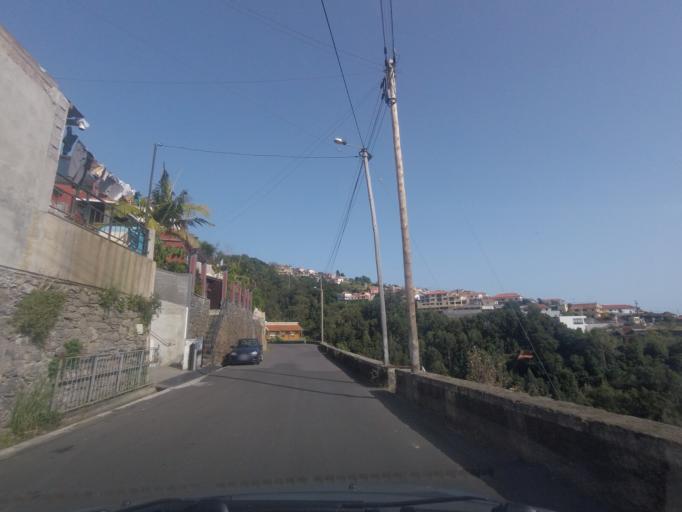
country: PT
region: Madeira
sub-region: Calheta
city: Arco da Calheta
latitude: 32.7265
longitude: -17.1543
